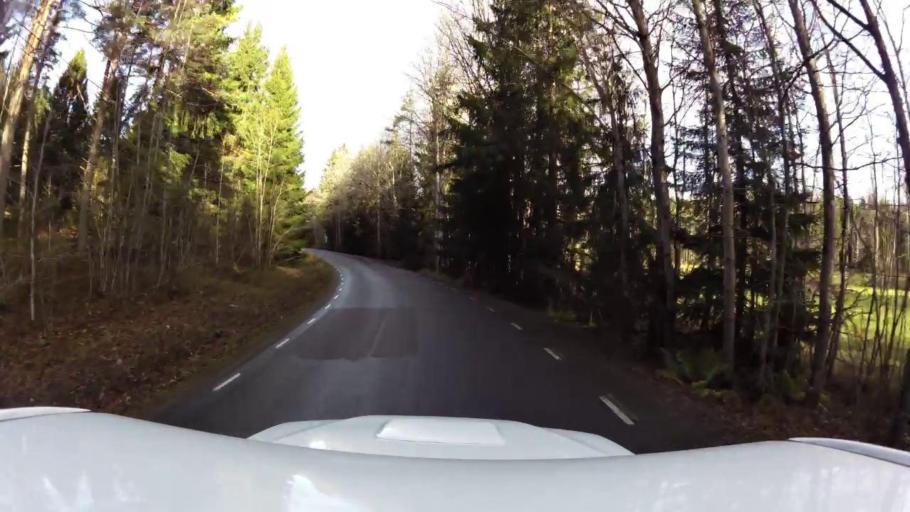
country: SE
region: OEstergoetland
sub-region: Linkopings Kommun
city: Sturefors
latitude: 58.3337
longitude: 15.6527
